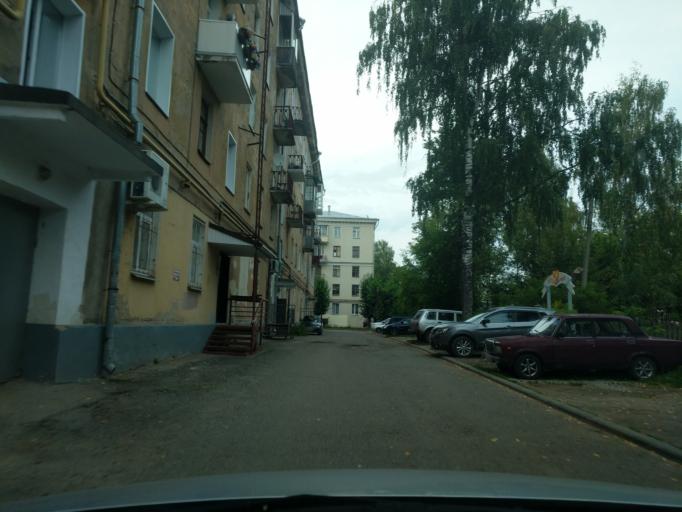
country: RU
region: Kirov
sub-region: Kirovo-Chepetskiy Rayon
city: Kirov
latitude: 58.6093
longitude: 49.6580
